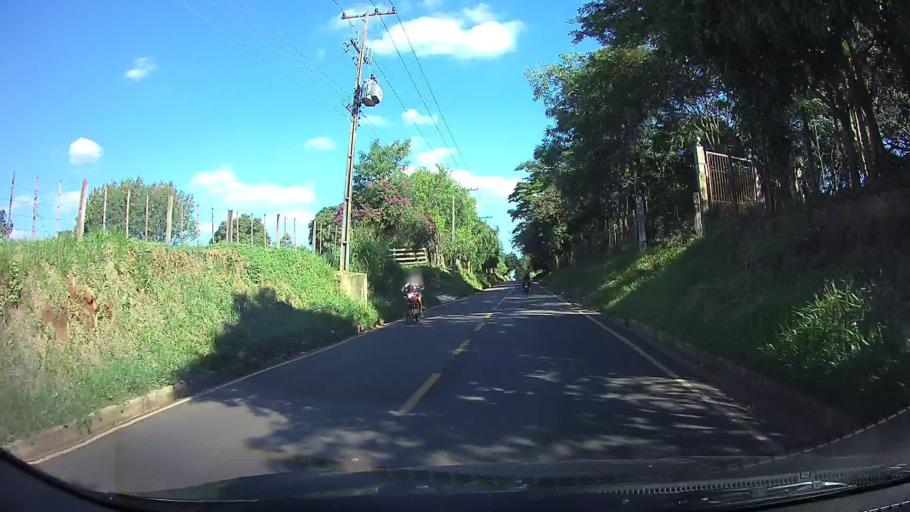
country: PY
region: Central
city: Limpio
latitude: -25.2015
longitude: -57.4788
